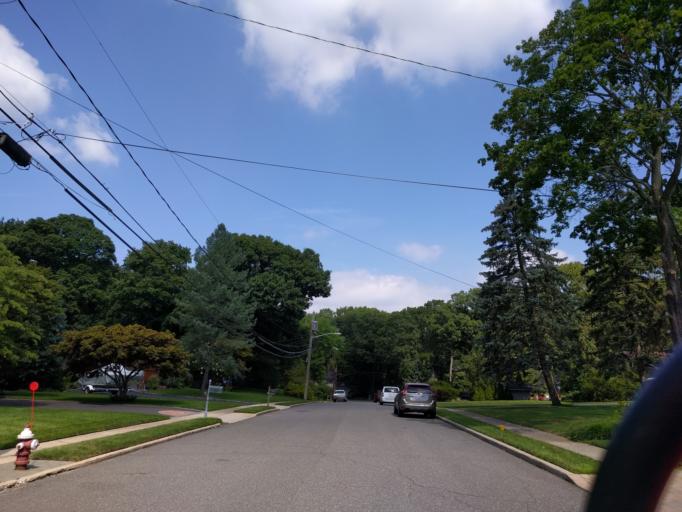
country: US
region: New York
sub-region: Nassau County
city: East Norwich
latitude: 40.8438
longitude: -73.5310
